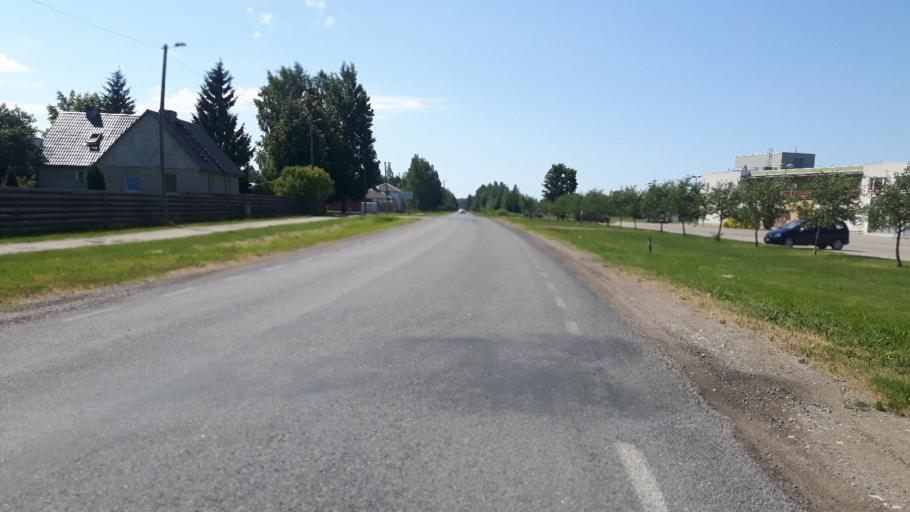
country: EE
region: Paernumaa
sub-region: Vaendra vald (alev)
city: Vandra
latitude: 58.6462
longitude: 25.0291
